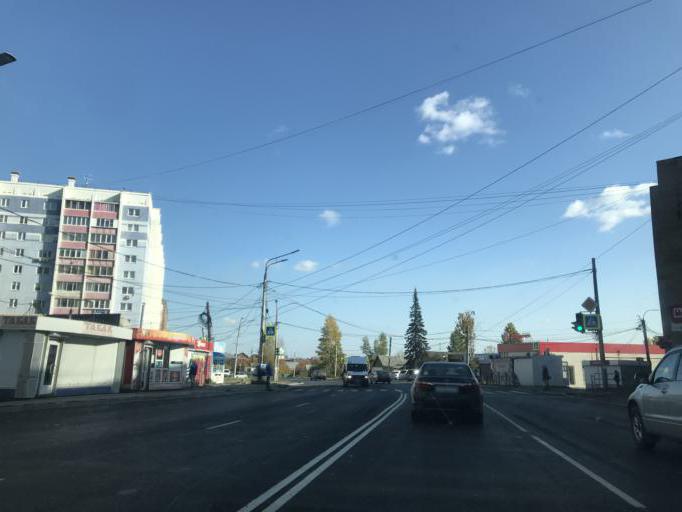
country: RU
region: Chelyabinsk
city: Roshchino
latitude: 55.2348
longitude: 61.2998
